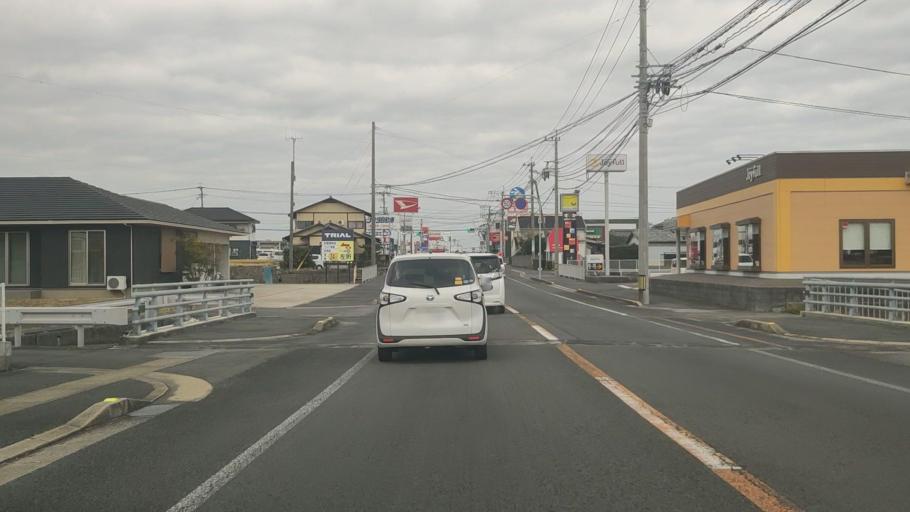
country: JP
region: Nagasaki
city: Shimabara
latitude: 32.8032
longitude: 130.3633
